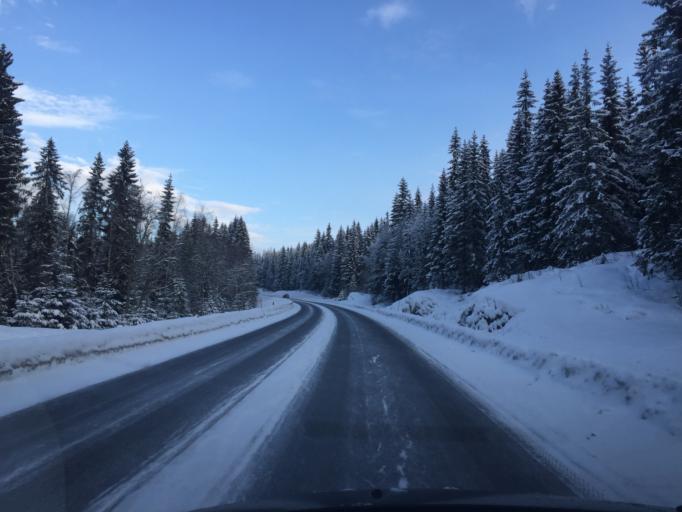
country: NO
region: Hedmark
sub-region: Trysil
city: Innbygda
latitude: 61.0908
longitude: 12.0006
